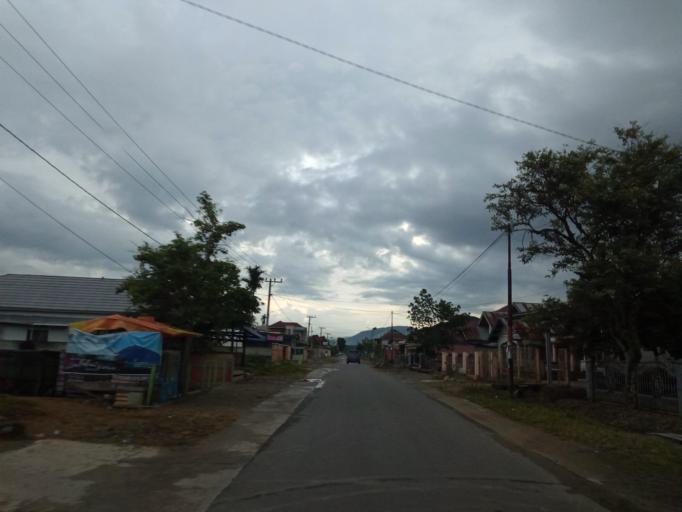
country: ID
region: Jambi
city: Semurup
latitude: -1.9884
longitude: 101.3590
